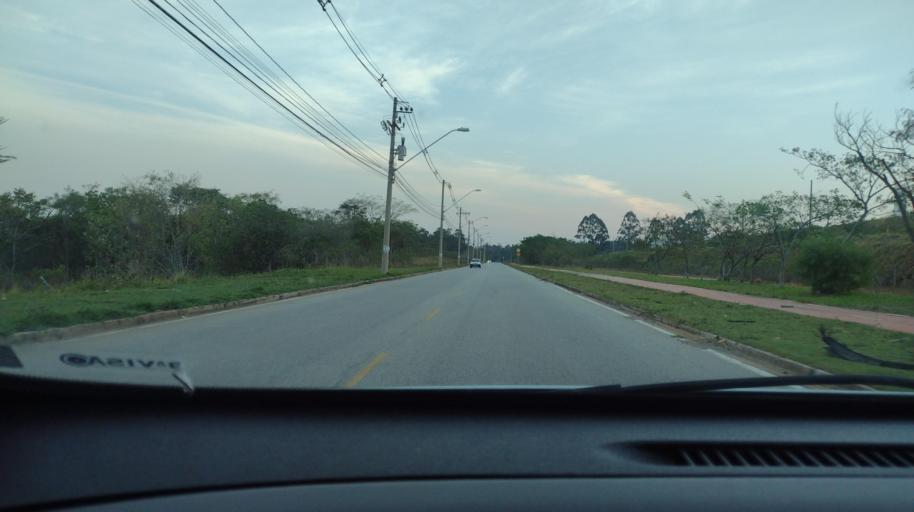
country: BR
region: Sao Paulo
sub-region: Sorocaba
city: Sorocaba
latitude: -23.3705
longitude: -47.4729
